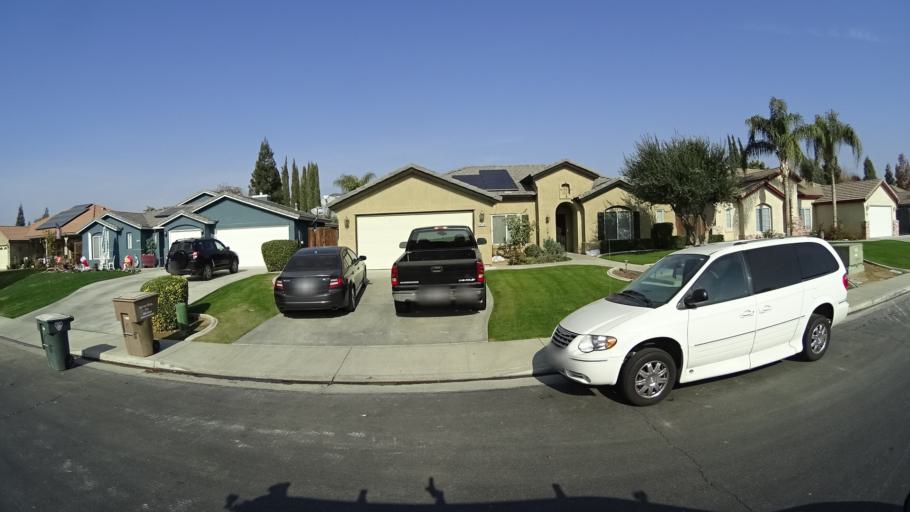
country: US
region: California
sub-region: Kern County
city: Greenacres
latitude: 35.4224
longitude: -119.1151
